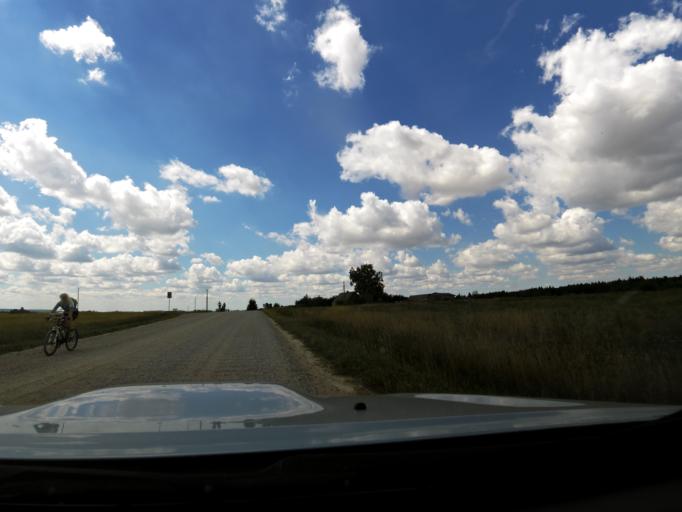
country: LT
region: Vilnius County
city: Elektrenai
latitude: 54.9085
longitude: 24.6419
